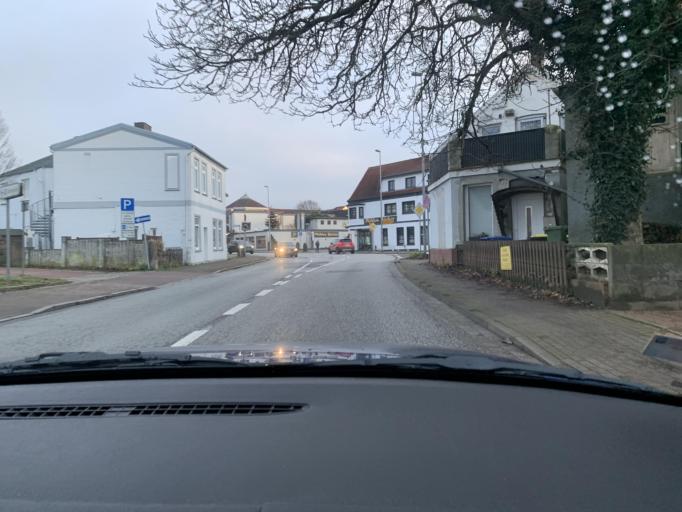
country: DE
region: Schleswig-Holstein
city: Wesseln
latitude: 54.1926
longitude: 9.0884
